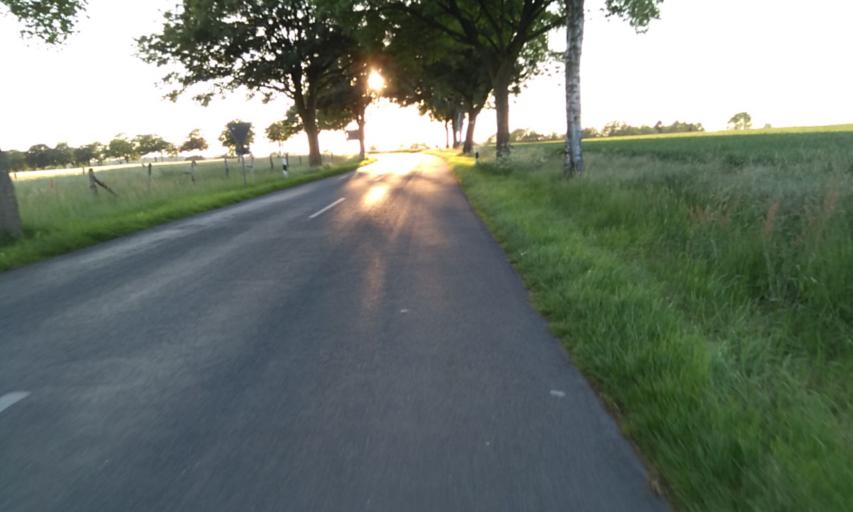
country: DE
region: Lower Saxony
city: Ahlerstedt
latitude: 53.4269
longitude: 9.4468
